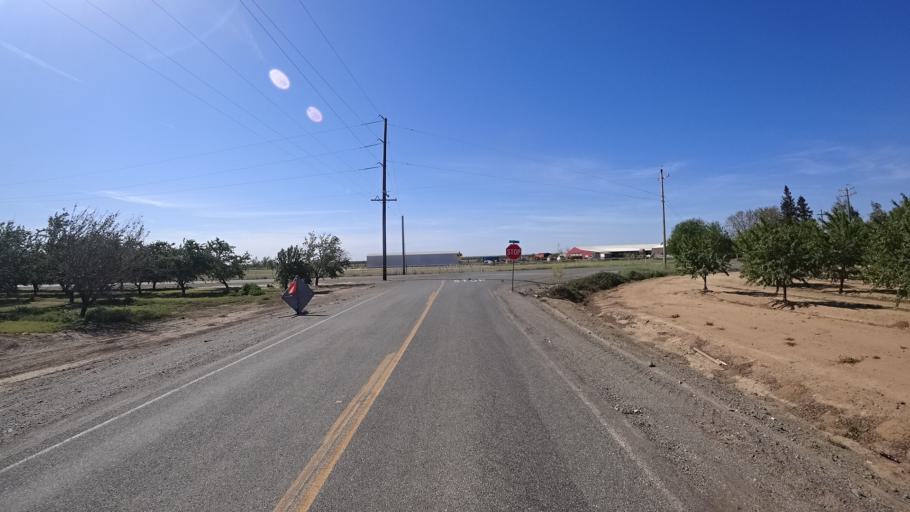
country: US
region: California
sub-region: Glenn County
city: Willows
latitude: 39.6244
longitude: -122.1788
